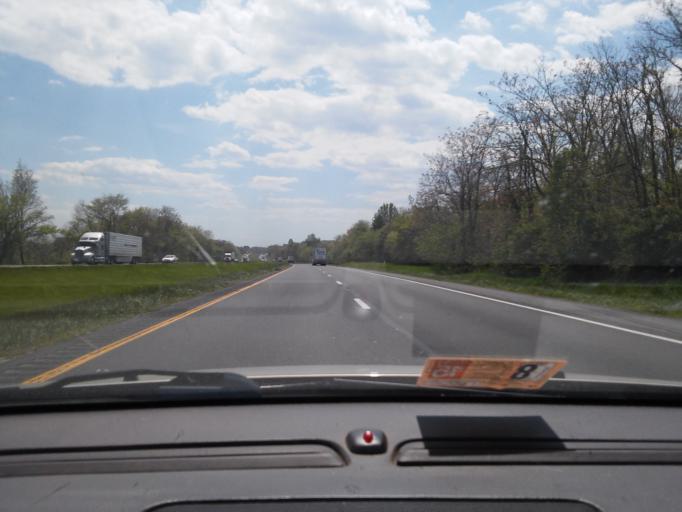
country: US
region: West Virginia
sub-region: Berkeley County
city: Inwood
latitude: 39.3479
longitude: -78.0583
